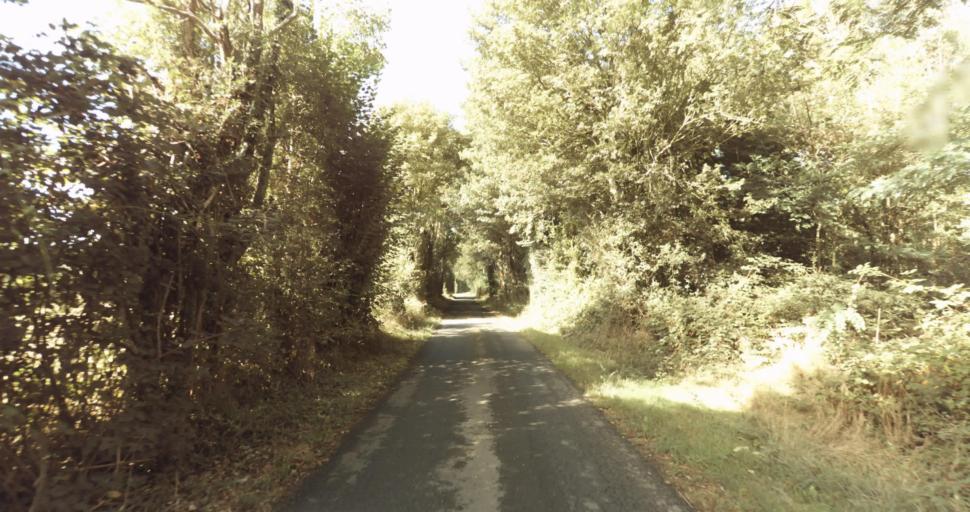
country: FR
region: Lower Normandy
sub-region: Departement de l'Orne
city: Vimoutiers
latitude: 48.9203
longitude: 0.1180
